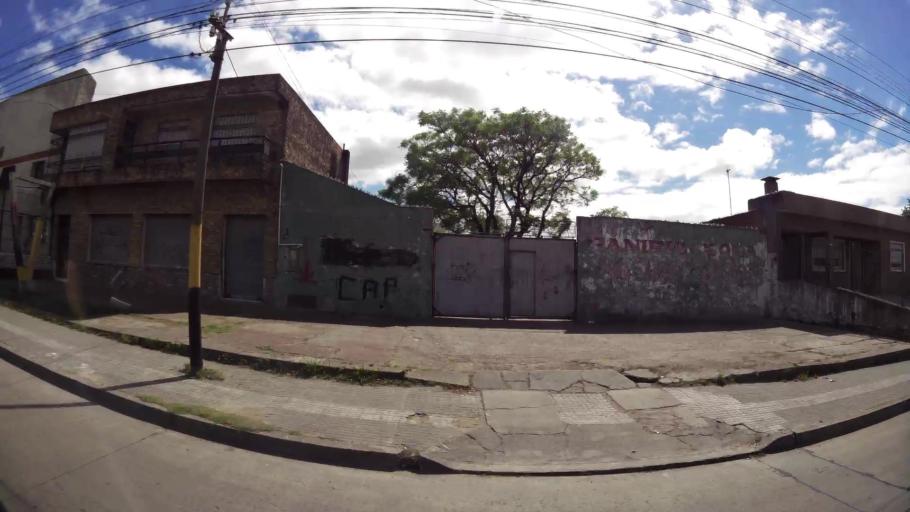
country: UY
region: Canelones
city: Paso de Carrasco
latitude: -34.8759
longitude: -56.1122
